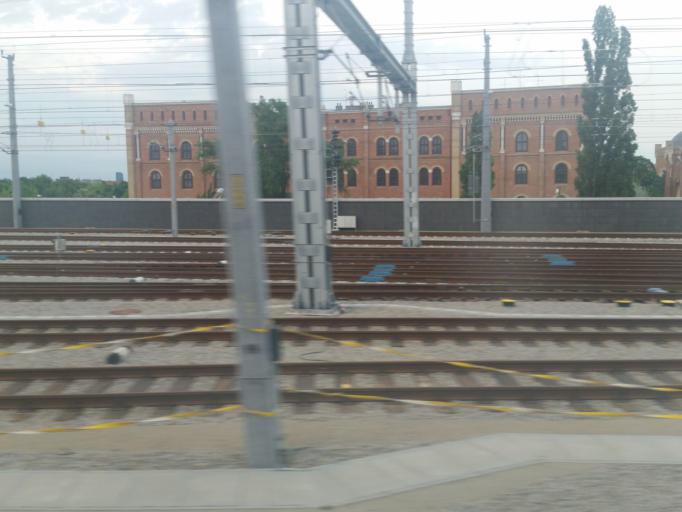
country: AT
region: Vienna
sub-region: Wien Stadt
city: Vienna
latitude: 48.1829
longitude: 16.3847
